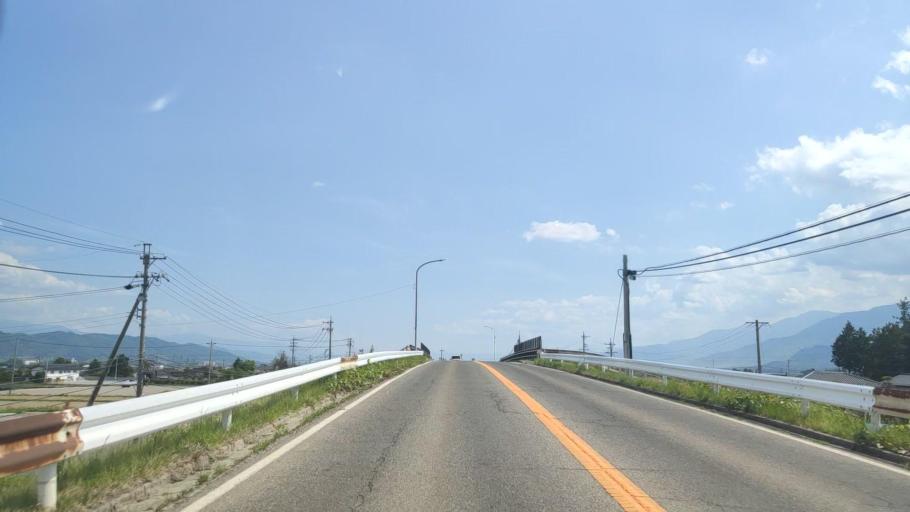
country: JP
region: Nagano
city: Omachi
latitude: 36.4516
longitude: 137.8523
